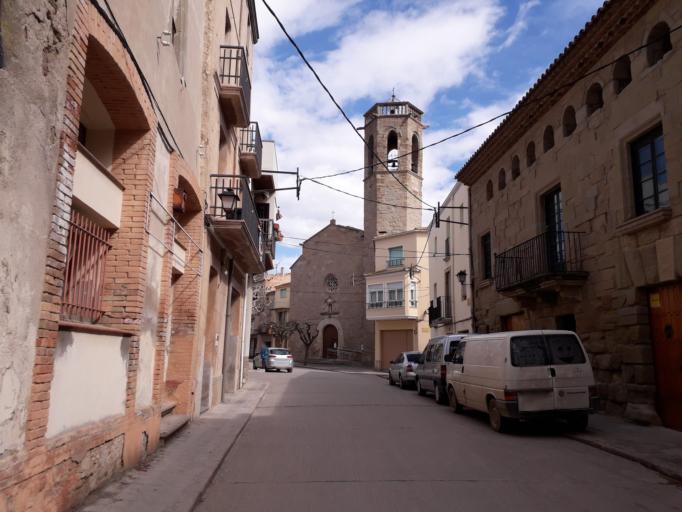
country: ES
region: Catalonia
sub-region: Provincia de Lleida
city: Castellsera
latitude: 41.7467
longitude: 0.9862
